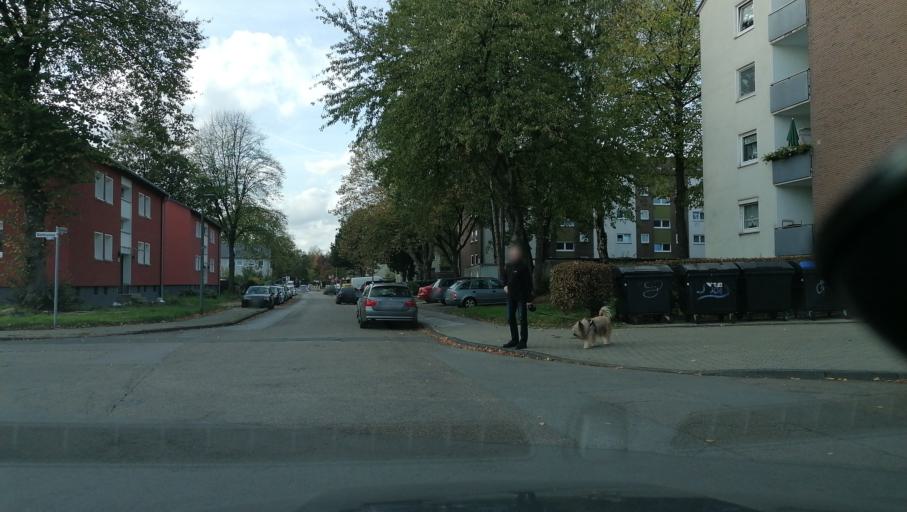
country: DE
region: North Rhine-Westphalia
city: Herten
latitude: 51.5817
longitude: 7.1192
